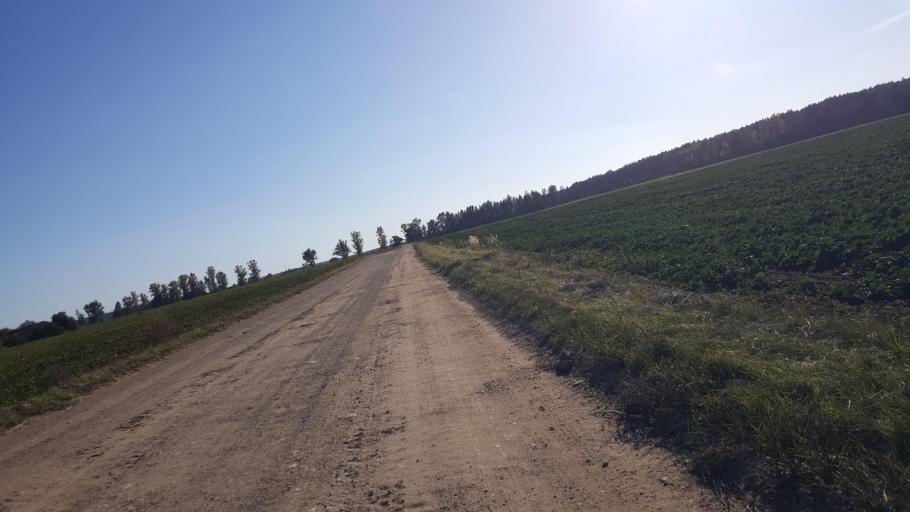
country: BY
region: Brest
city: Kamyanyets
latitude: 52.3798
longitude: 23.8809
